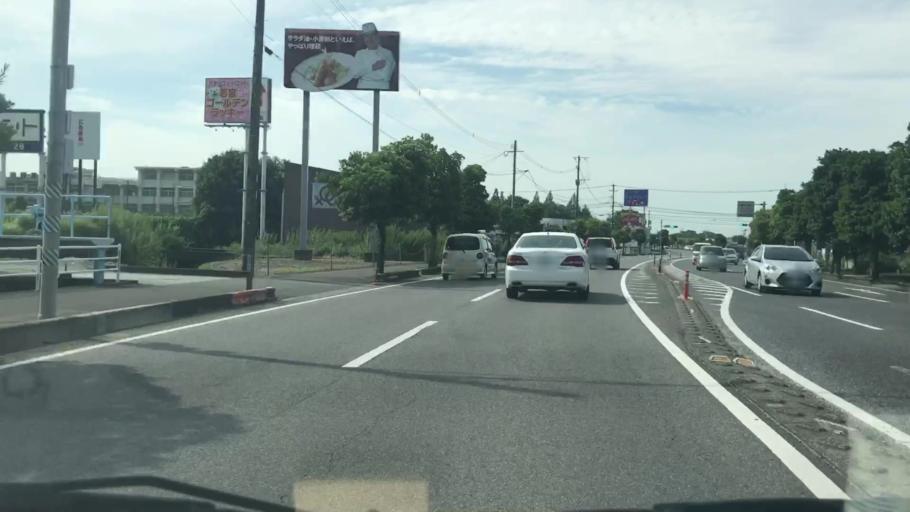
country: JP
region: Saga Prefecture
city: Saga-shi
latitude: 33.3163
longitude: 130.2763
